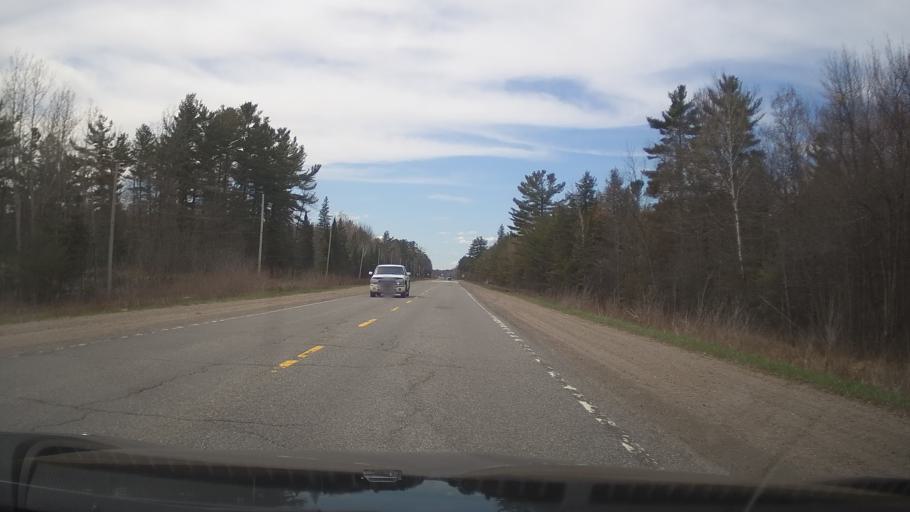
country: CA
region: Ontario
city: Arnprior
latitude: 45.5309
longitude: -76.3092
